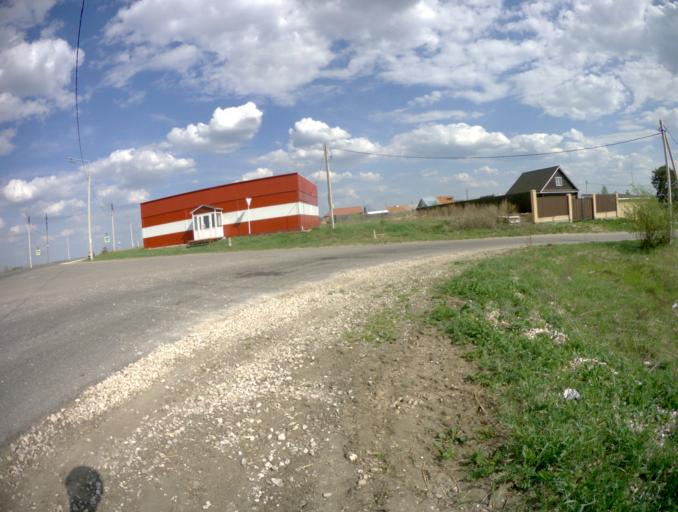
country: RU
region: Vladimir
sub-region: Kovrovskiy Rayon
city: Kovrov
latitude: 56.4435
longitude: 41.2737
